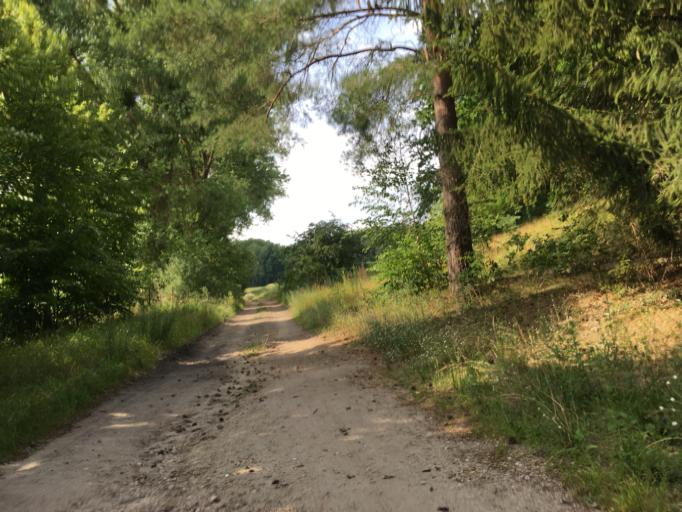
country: DE
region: Brandenburg
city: Rudnitz
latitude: 52.7314
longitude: 13.5871
